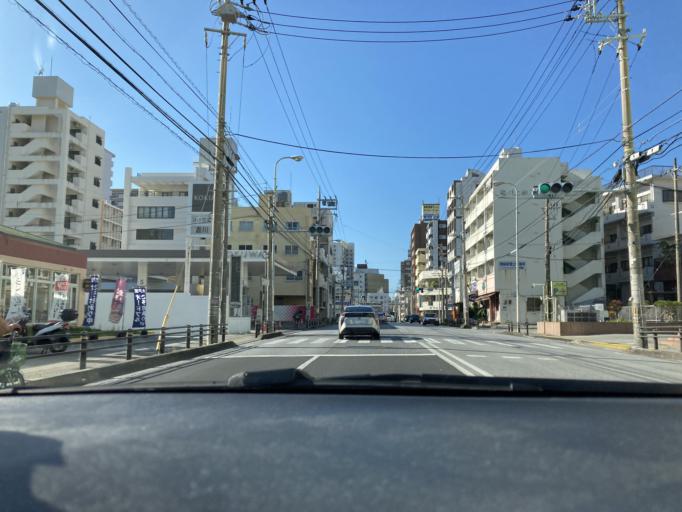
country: JP
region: Okinawa
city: Naha-shi
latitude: 26.2063
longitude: 127.6803
